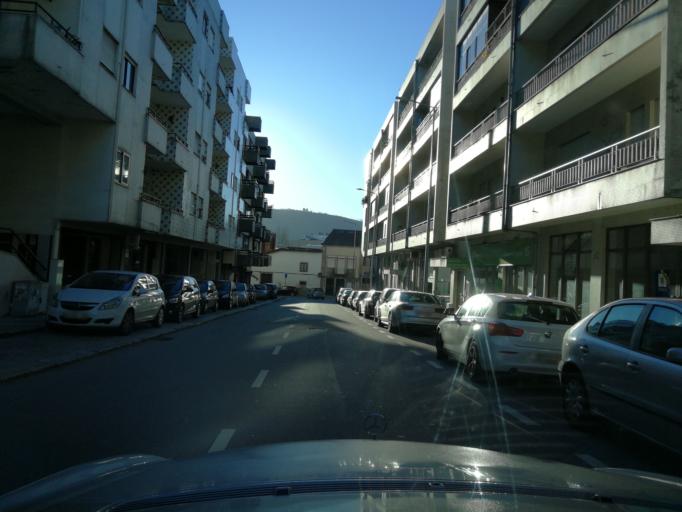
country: PT
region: Braga
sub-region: Braga
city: Braga
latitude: 41.5547
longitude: -8.4102
